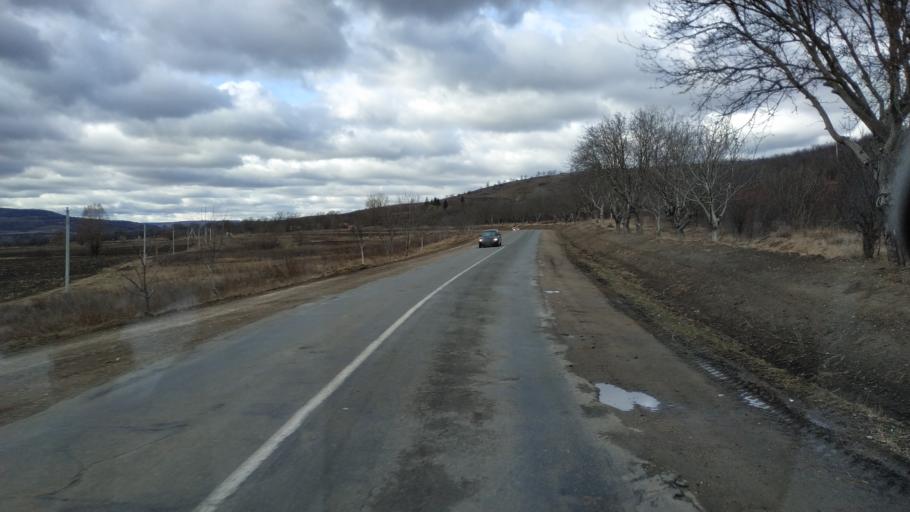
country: MD
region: Stinga Nistrului
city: Bucovat
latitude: 47.1700
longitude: 28.4446
